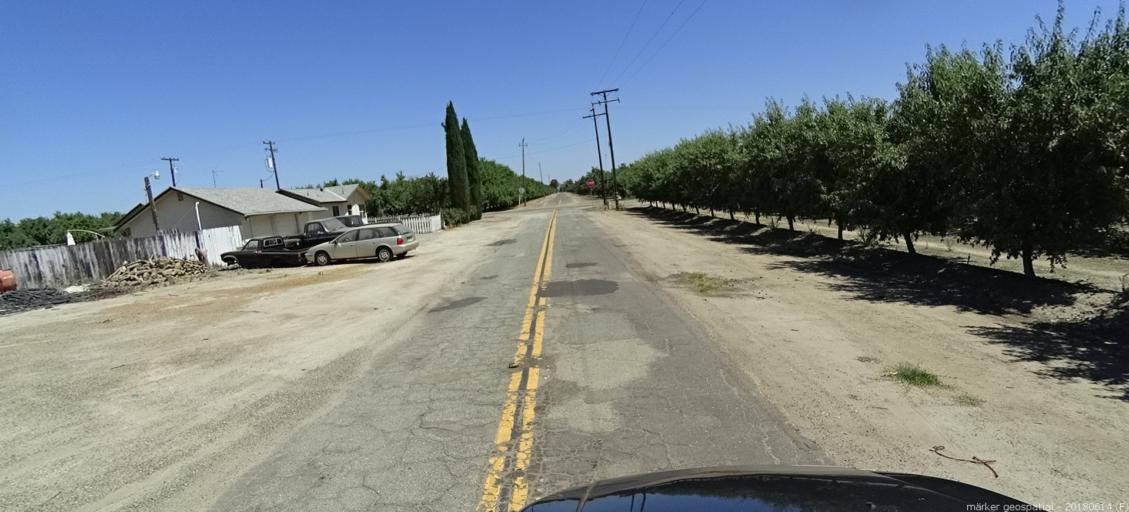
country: US
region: California
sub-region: Madera County
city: Fairmead
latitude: 36.9958
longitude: -120.2476
